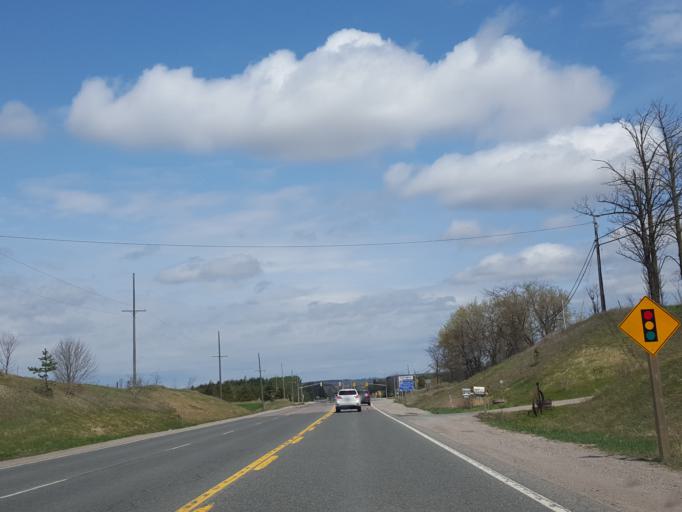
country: CA
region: Ontario
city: Newmarket
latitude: 44.1085
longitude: -79.3143
